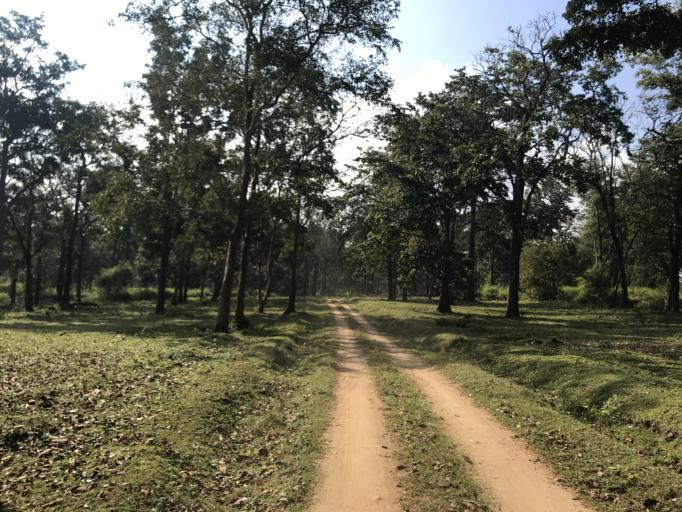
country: IN
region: Karnataka
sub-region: Mysore
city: Heggadadevankote
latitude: 11.9486
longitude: 76.2186
